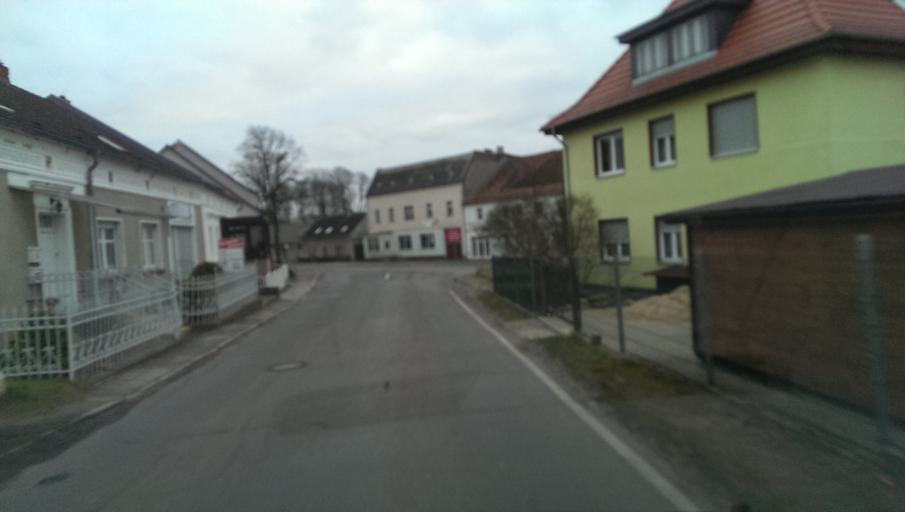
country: DE
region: Brandenburg
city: Sperenberg
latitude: 52.1424
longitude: 13.3651
